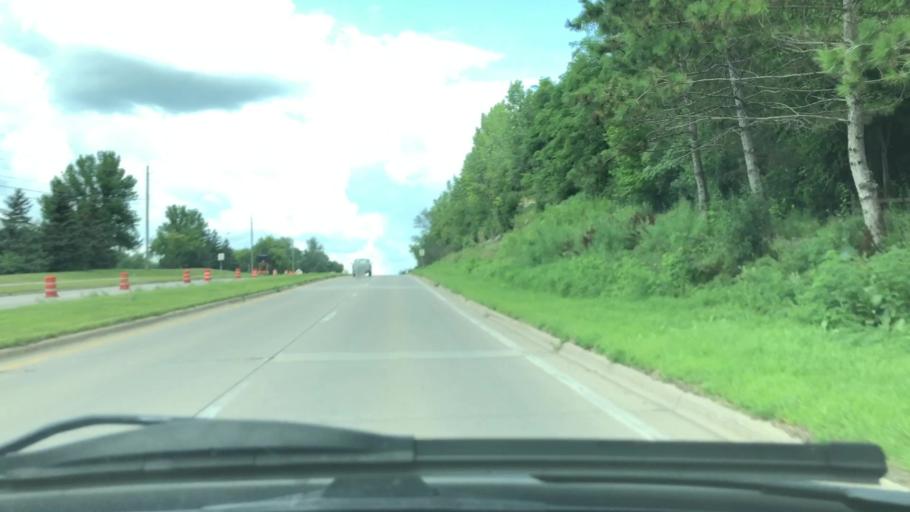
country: US
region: Minnesota
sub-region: Olmsted County
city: Rochester
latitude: 44.0284
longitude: -92.5163
